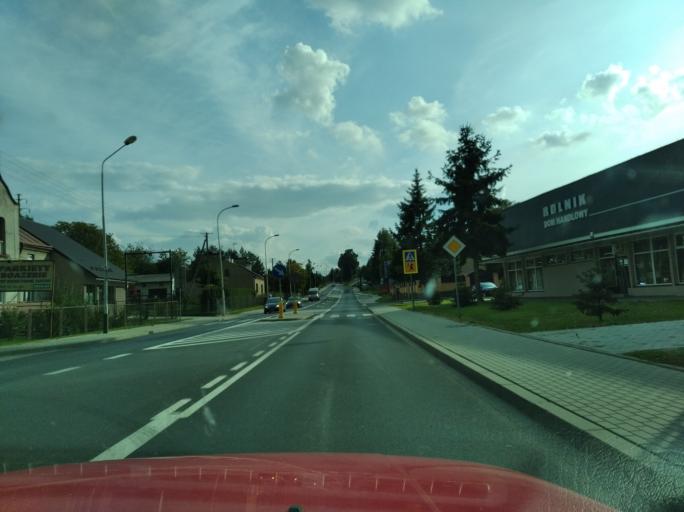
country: PL
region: Subcarpathian Voivodeship
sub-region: Powiat jaroslawski
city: Jaroslaw
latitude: 50.0065
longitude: 22.6756
